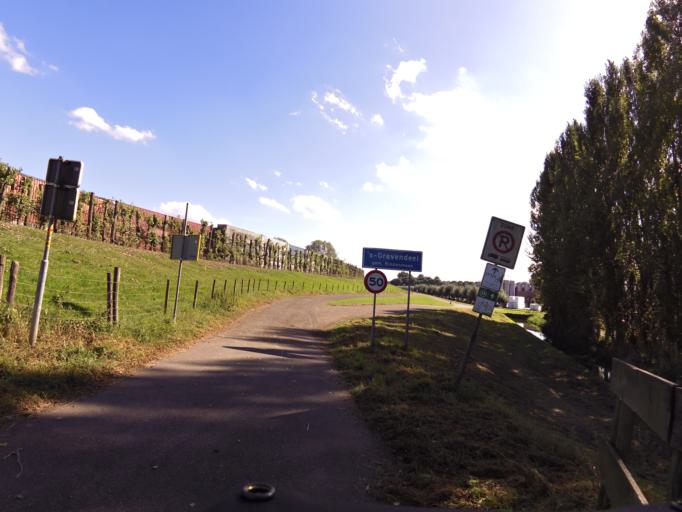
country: NL
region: South Holland
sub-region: Gemeente Zwijndrecht
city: Zwijndrecht
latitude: 51.7862
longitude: 4.6215
